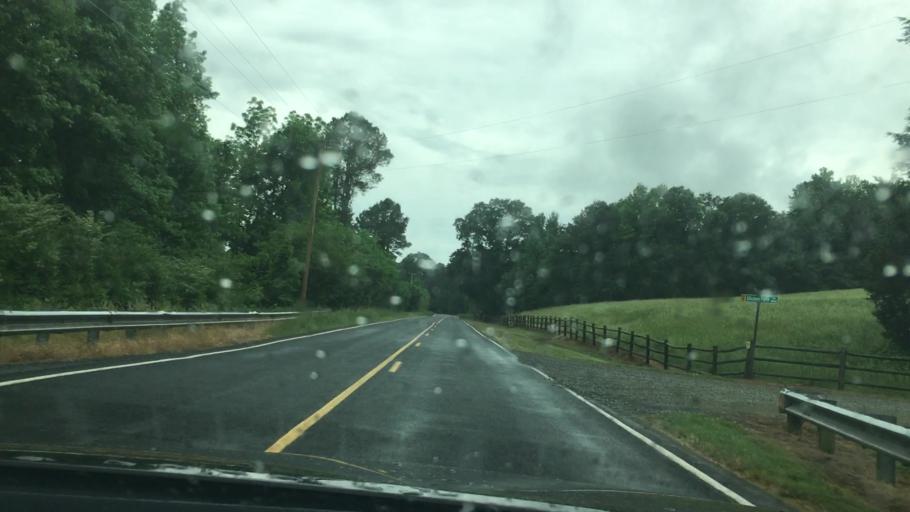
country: US
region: North Carolina
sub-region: Stanly County
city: Badin
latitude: 35.3638
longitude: -80.1162
